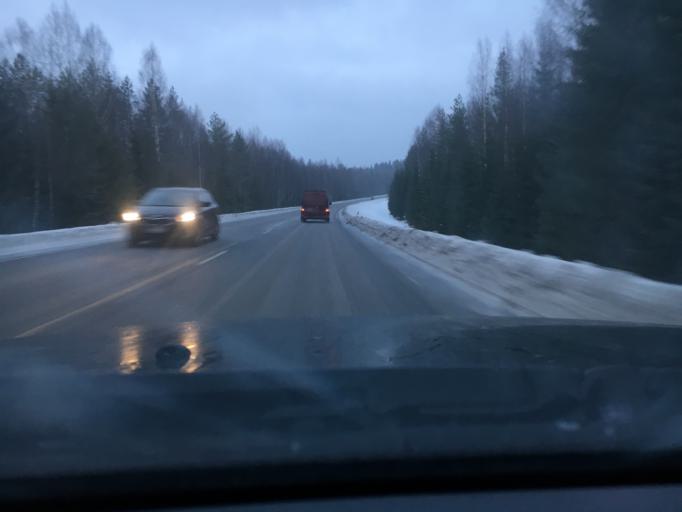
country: FI
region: Central Finland
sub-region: Jyvaeskylae
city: Hankasalmi
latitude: 62.4126
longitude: 26.6927
